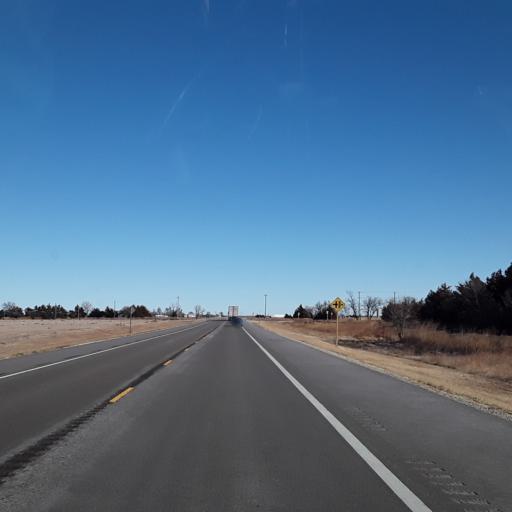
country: US
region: Kansas
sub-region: Pawnee County
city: Larned
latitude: 38.1923
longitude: -99.0797
